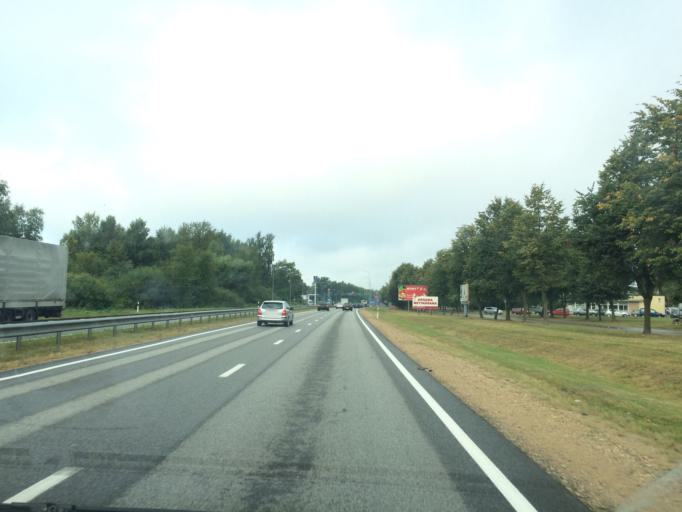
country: LV
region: Salaspils
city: Salaspils
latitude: 56.8502
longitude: 24.3406
